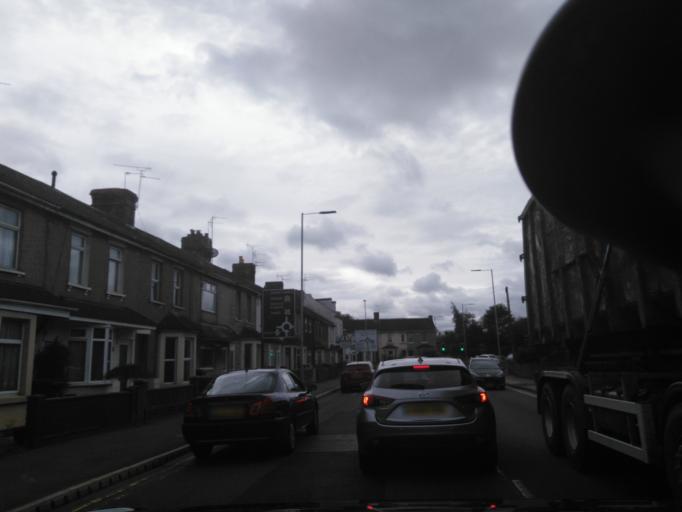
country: GB
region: England
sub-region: Borough of Swindon
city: Swindon
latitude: 51.5700
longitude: -1.8012
